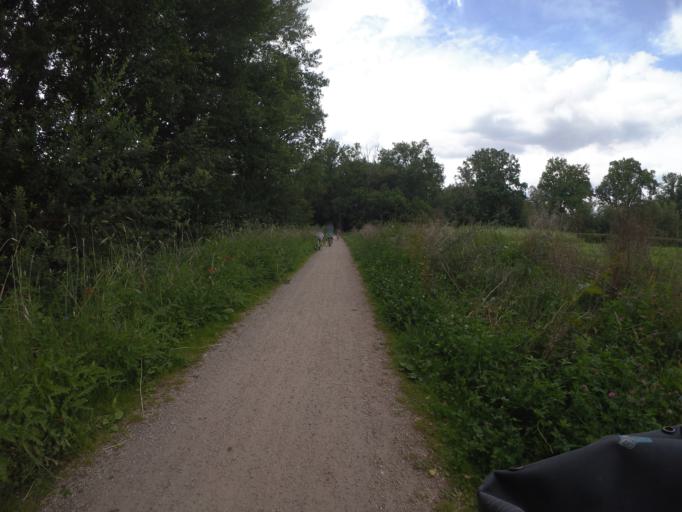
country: NL
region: North Brabant
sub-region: Gemeente Heeze-Leende
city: Heeze
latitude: 51.3964
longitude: 5.5898
